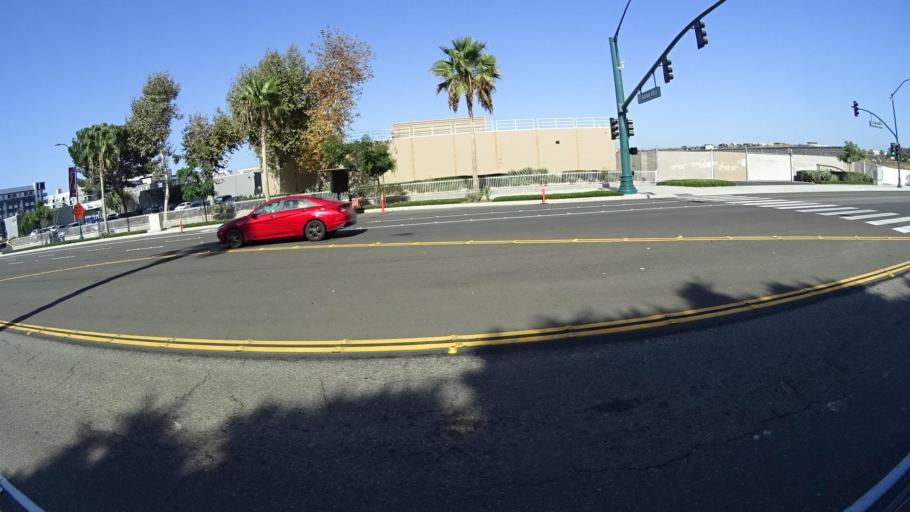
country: US
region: California
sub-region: Orange County
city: Orange
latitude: 33.8017
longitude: -117.8913
